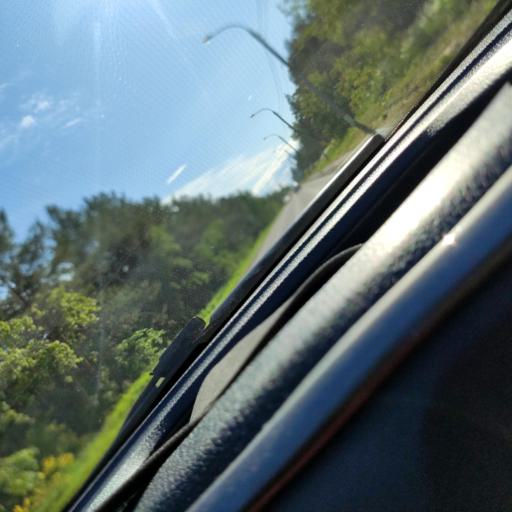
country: RU
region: Samara
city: Tol'yatti
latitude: 53.4760
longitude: 49.4244
